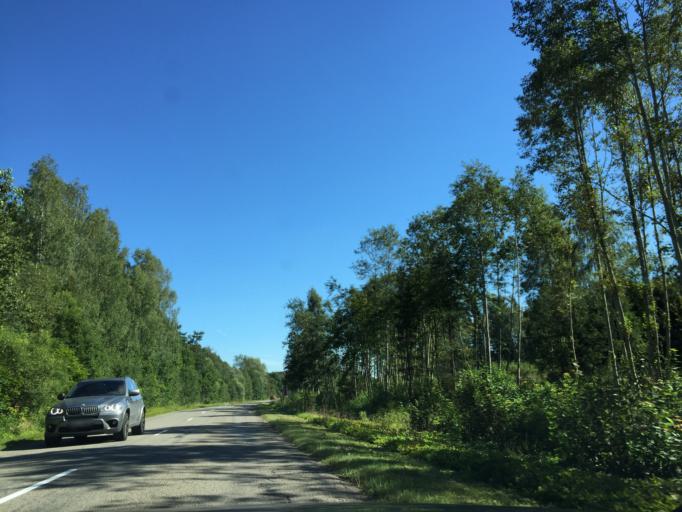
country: LV
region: Akniste
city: Akniste
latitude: 56.1120
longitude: 25.8443
